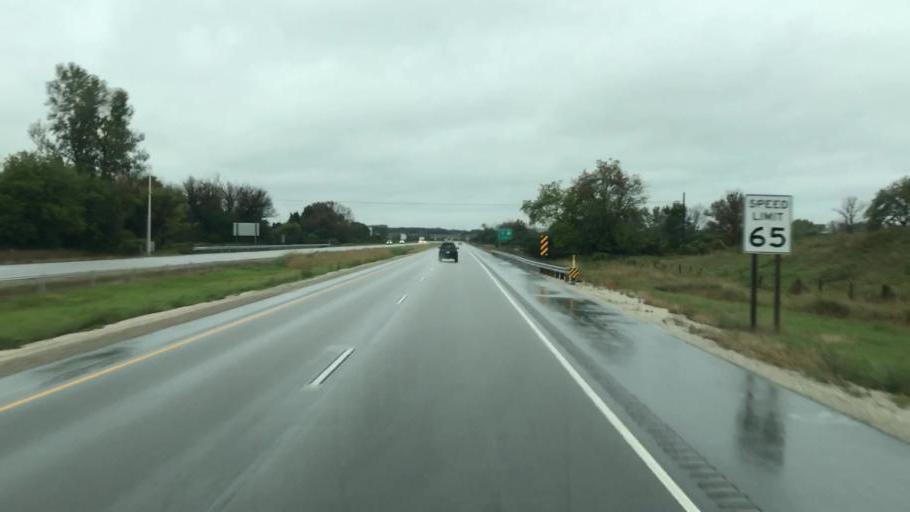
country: US
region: Wisconsin
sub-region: Waukesha County
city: Pewaukee
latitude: 43.0606
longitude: -88.2513
